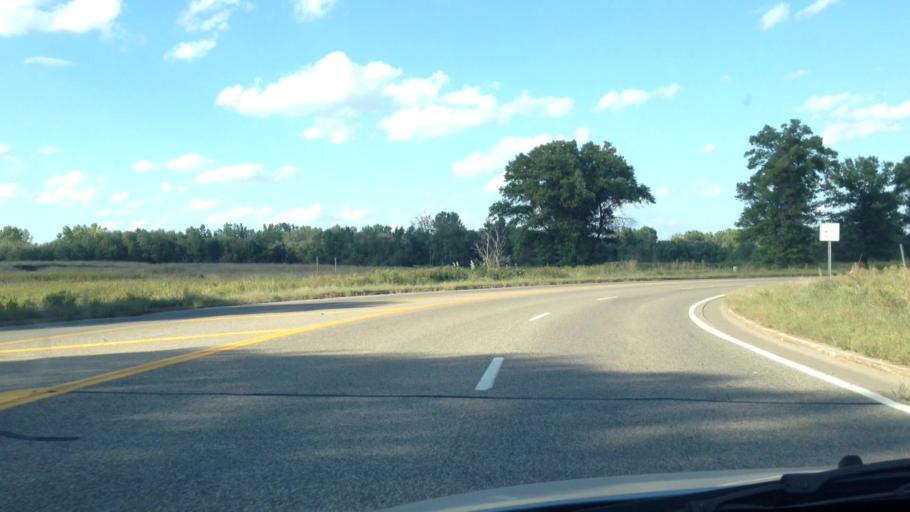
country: US
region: Minnesota
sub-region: Ramsey County
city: Mounds View
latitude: 45.1258
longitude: -93.1929
